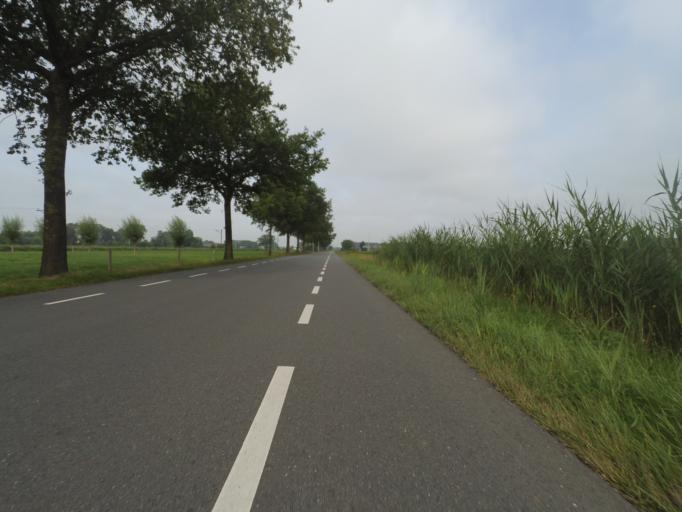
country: NL
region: Gelderland
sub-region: Gemeente Barneveld
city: Barneveld
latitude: 52.1208
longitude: 5.6145
